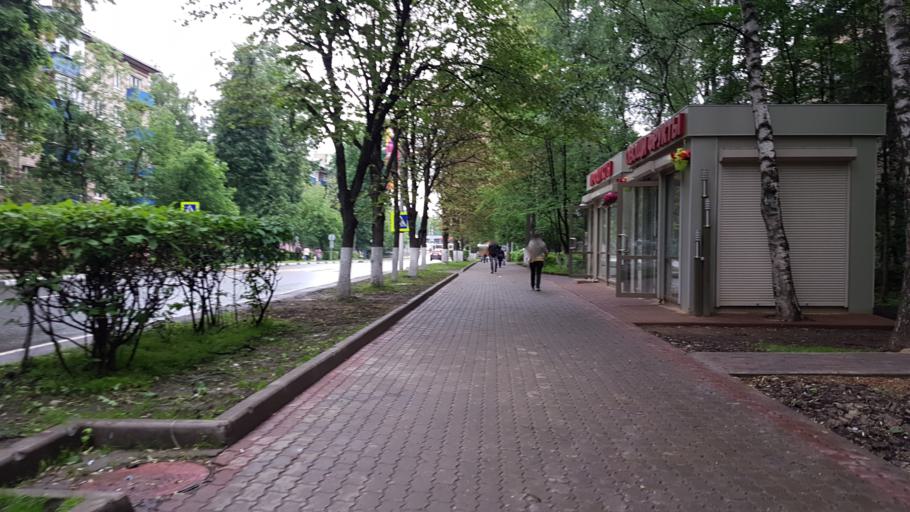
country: RU
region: Moscow
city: Khimki
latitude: 55.8919
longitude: 37.4483
